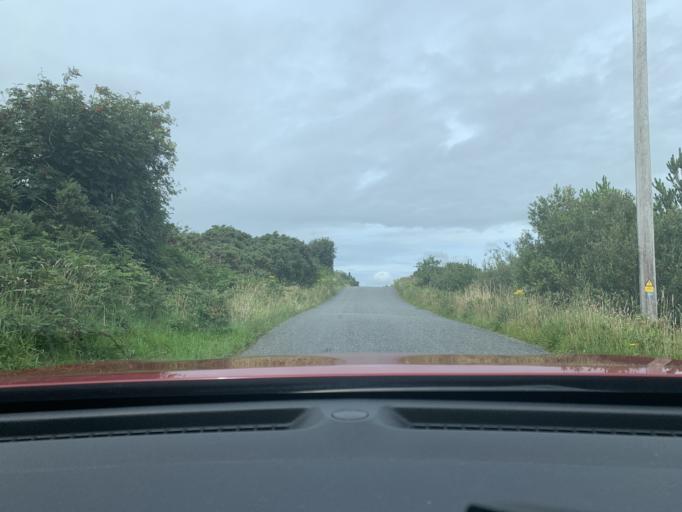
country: IE
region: Ulster
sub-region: County Donegal
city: Dungloe
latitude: 54.9412
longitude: -8.3590
